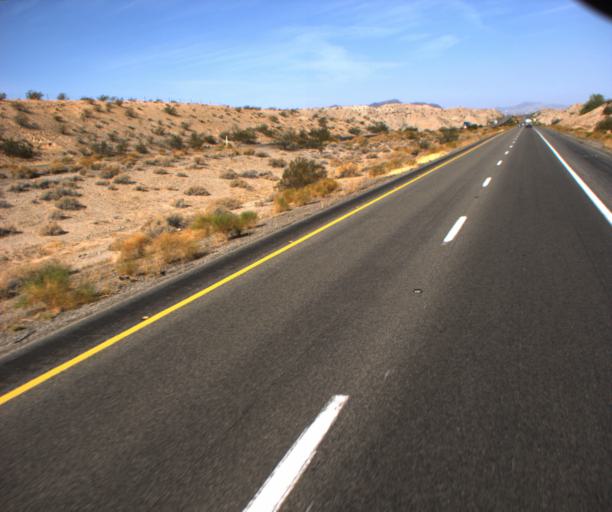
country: US
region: Arizona
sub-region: Mohave County
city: Desert Hills
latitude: 34.7267
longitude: -114.3976
